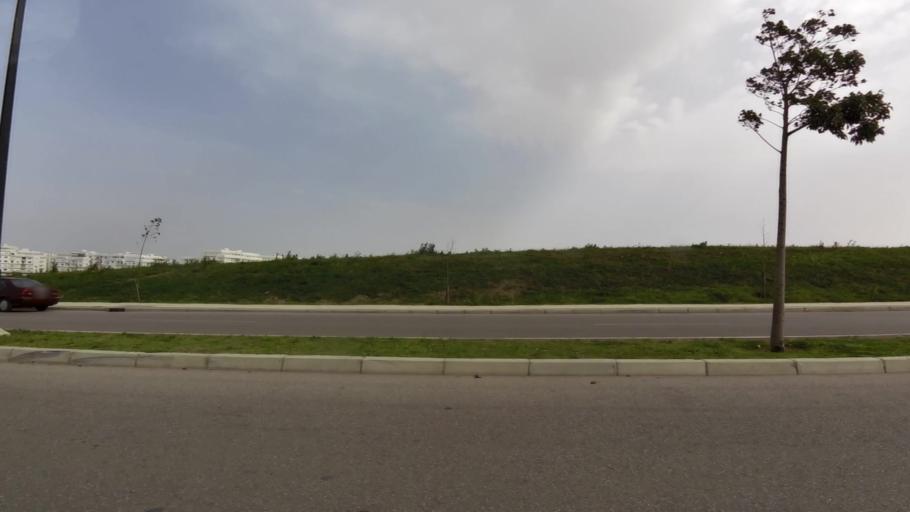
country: MA
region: Tanger-Tetouan
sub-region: Tanger-Assilah
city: Boukhalef
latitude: 35.7438
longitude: -5.8540
